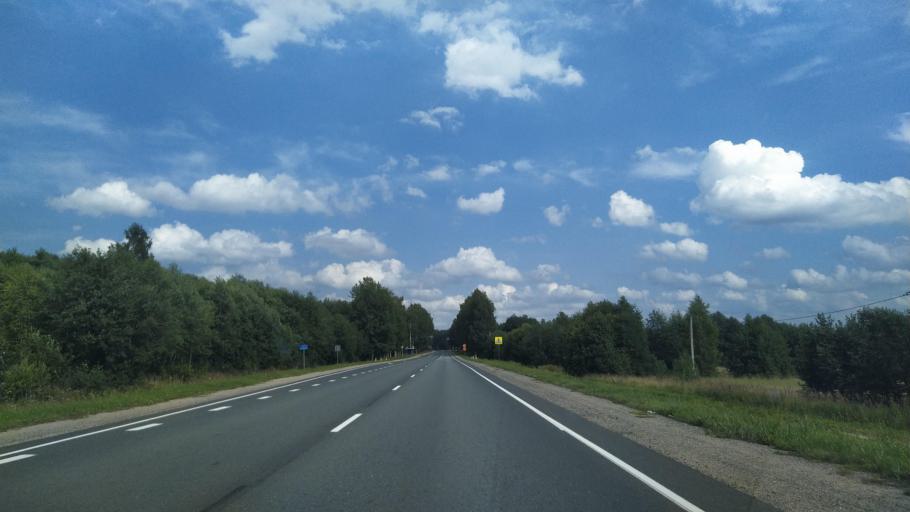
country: RU
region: Pskov
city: Dno
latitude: 57.9831
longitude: 29.7771
